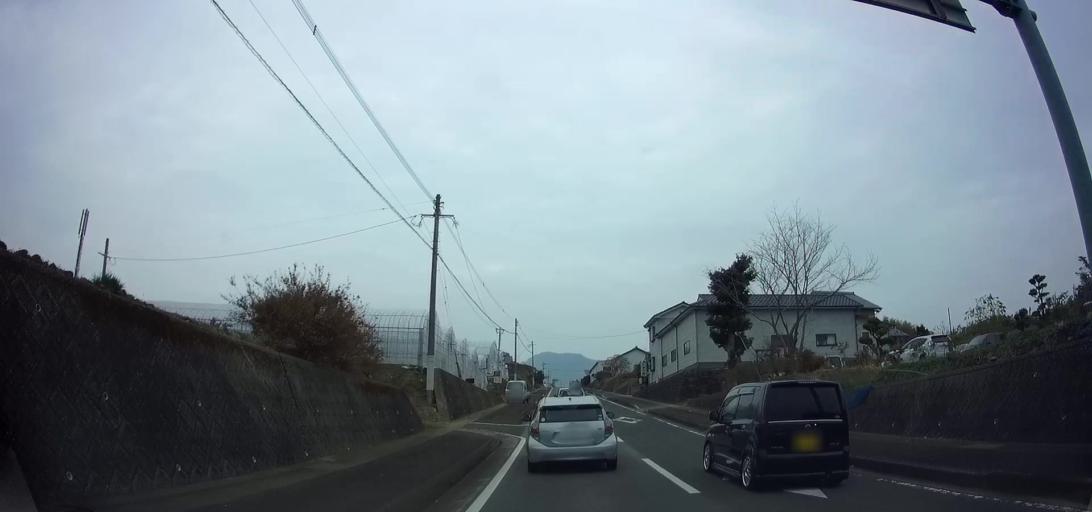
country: JP
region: Nagasaki
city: Shimabara
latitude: 32.6599
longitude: 130.2883
